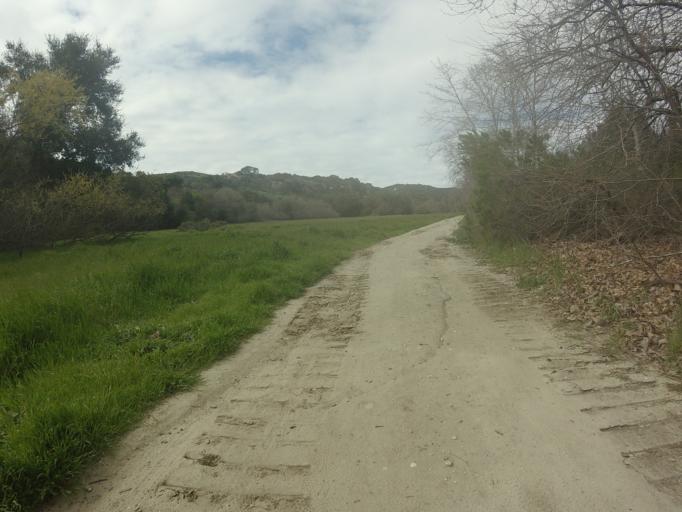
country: US
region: California
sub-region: Orange County
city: Aliso Viejo
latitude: 33.5599
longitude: -117.7427
